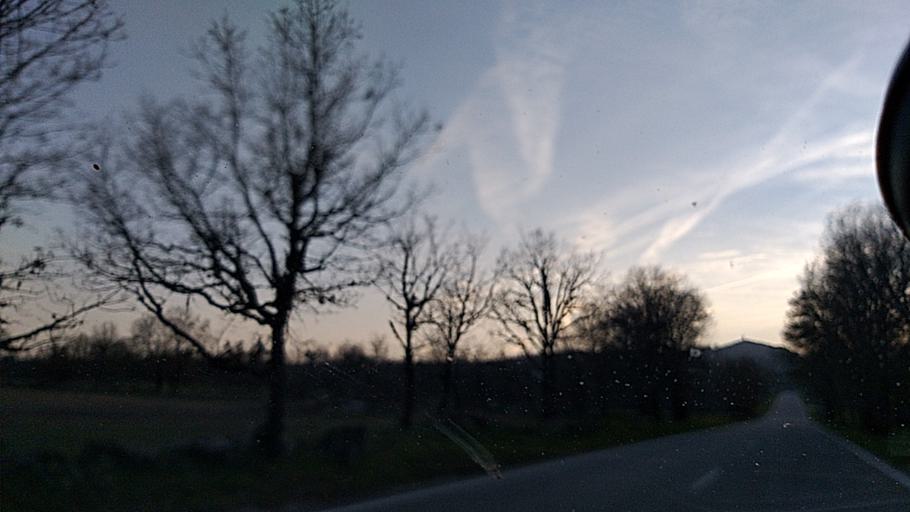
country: PT
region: Guarda
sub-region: Guarda
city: Sequeira
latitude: 40.5977
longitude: -7.1185
